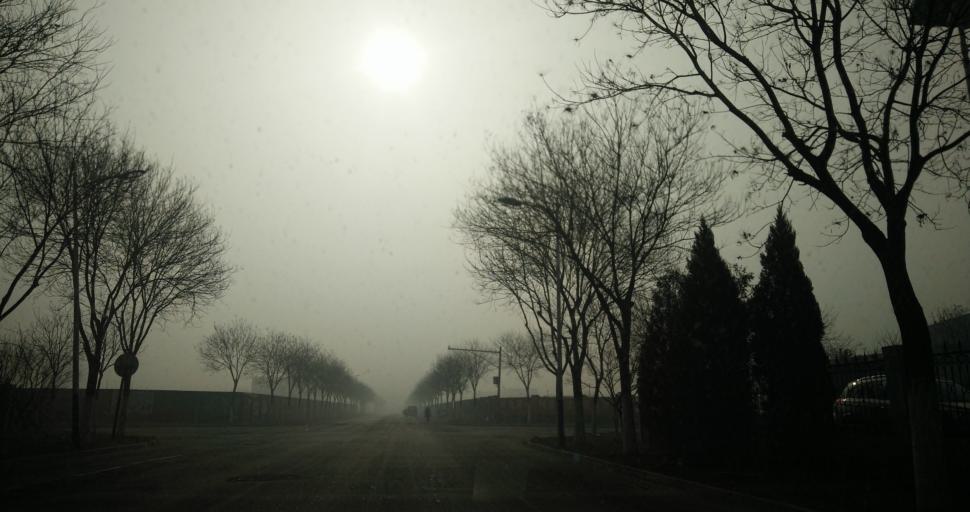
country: CN
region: Beijing
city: Yinghai
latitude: 39.7445
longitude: 116.4426
